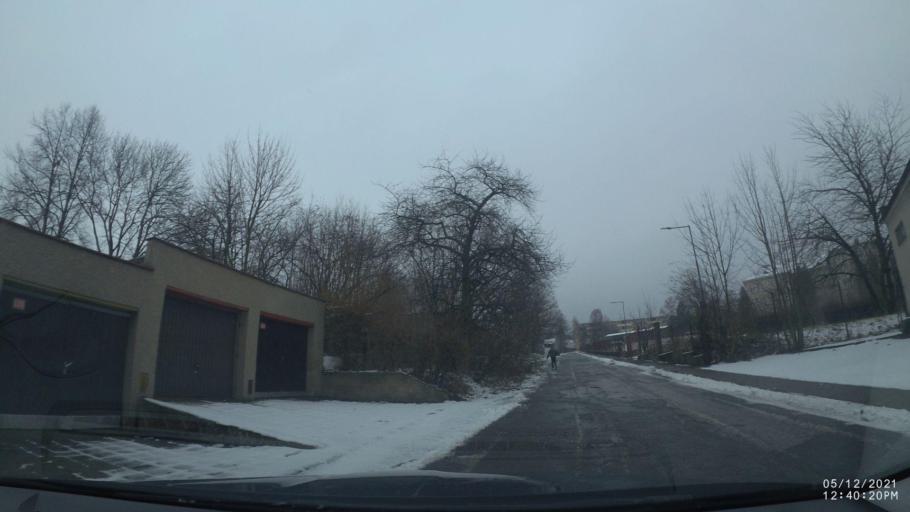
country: CZ
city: Nove Mesto nad Metuji
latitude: 50.3557
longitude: 16.1503
